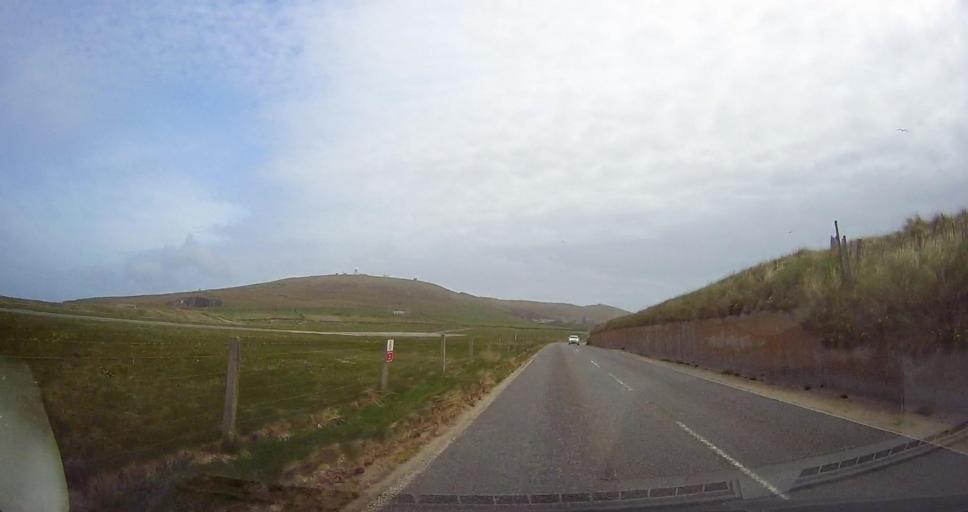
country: GB
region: Scotland
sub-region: Shetland Islands
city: Sandwick
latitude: 59.8742
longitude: -1.2905
